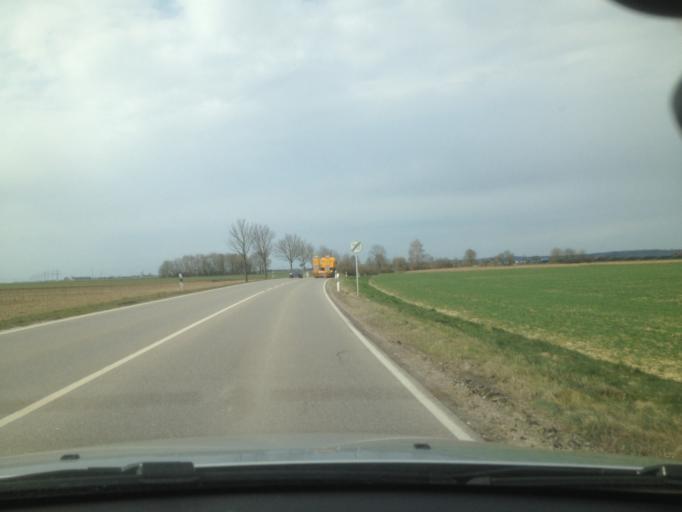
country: DE
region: Bavaria
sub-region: Swabia
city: Bobingen
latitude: 48.2562
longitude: 10.8417
